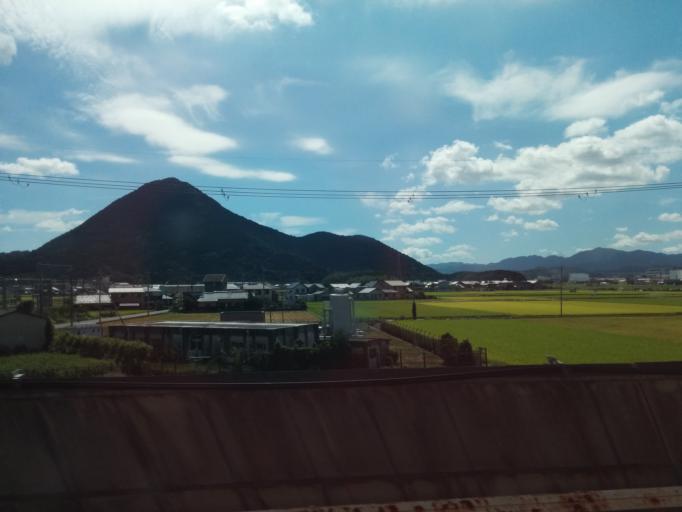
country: JP
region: Shiga Prefecture
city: Moriyama
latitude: 35.0590
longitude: 136.0194
